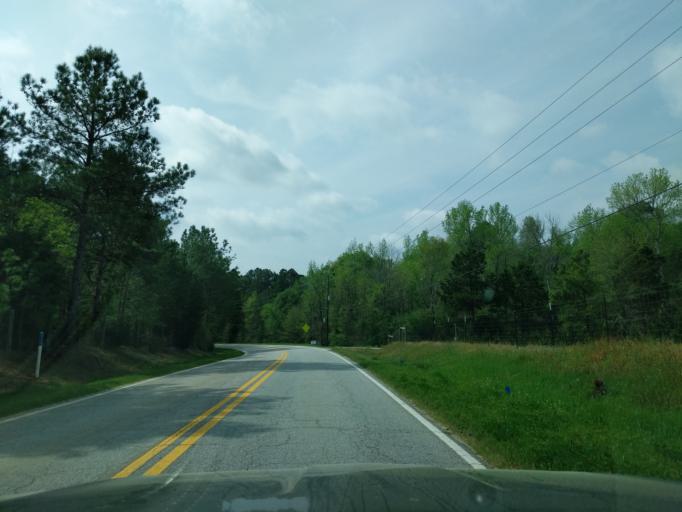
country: US
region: Georgia
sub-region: Columbia County
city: Appling
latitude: 33.5976
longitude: -82.3203
